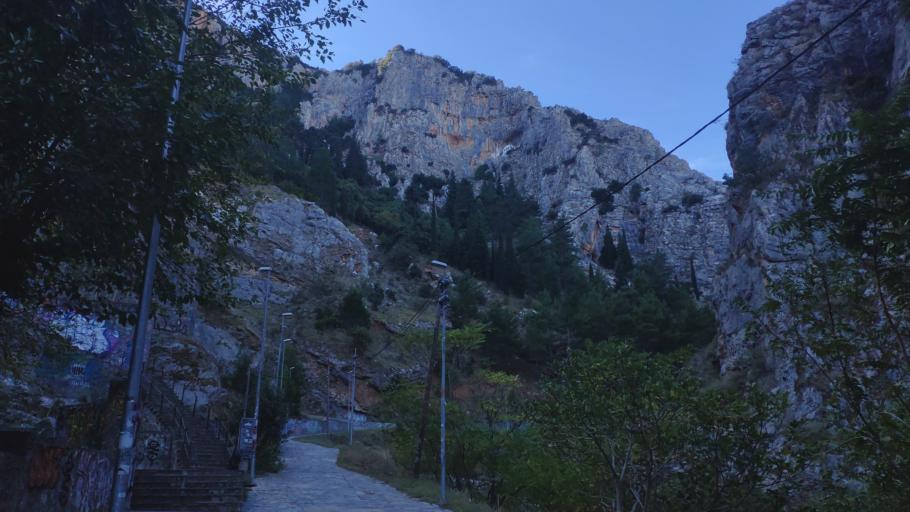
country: GR
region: Central Greece
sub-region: Nomos Voiotias
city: Livadeia
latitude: 38.4300
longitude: 22.8750
